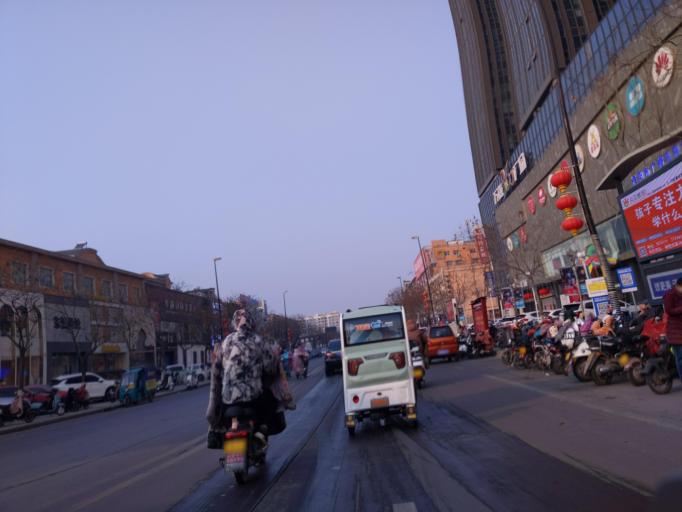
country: CN
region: Henan Sheng
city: Zhongyuanlu
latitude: 35.7714
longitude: 115.0590
